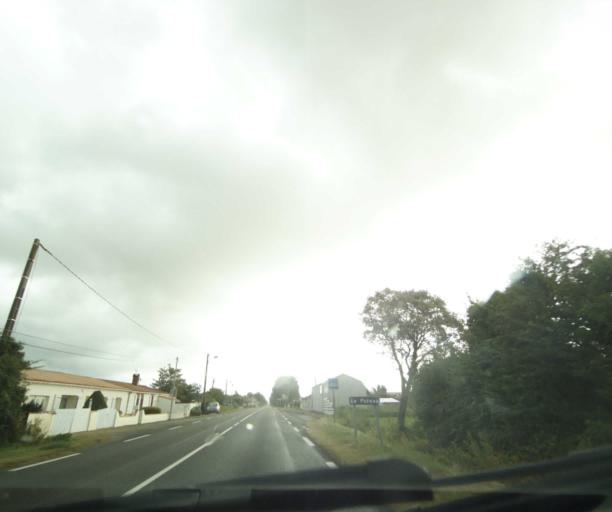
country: FR
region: Pays de la Loire
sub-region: Departement de la Vendee
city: Saint-Hilaire-de-Talmont
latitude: 46.4711
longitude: -1.5564
